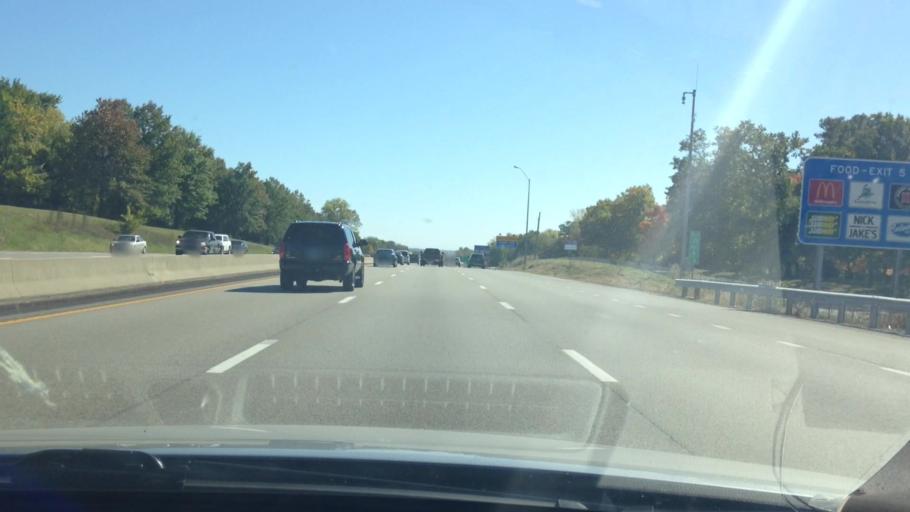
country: US
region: Missouri
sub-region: Platte County
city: Parkville
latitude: 39.2217
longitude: -94.6487
